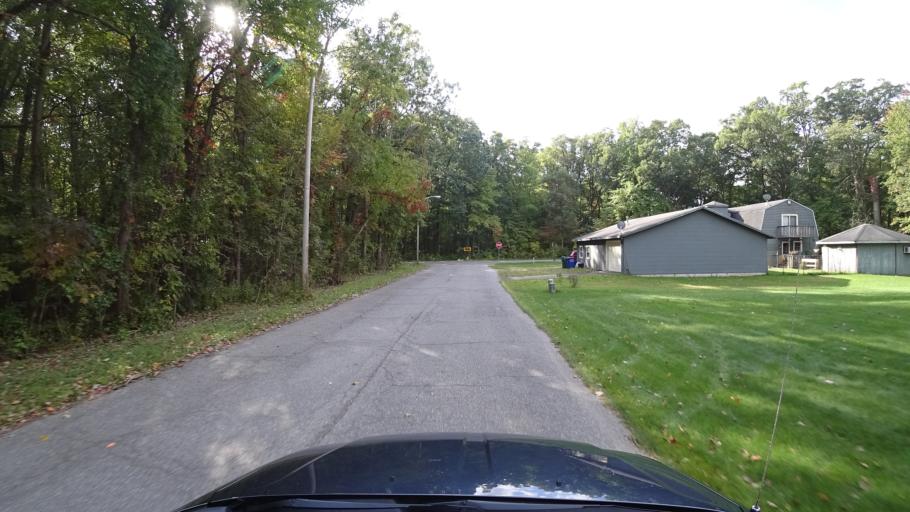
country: US
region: Indiana
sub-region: LaPorte County
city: Trail Creek
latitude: 41.6918
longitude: -86.8714
